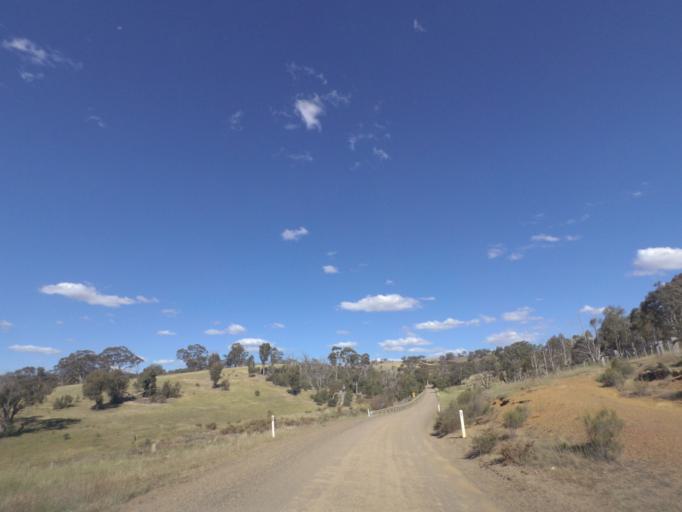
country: AU
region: Victoria
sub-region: Hume
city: Craigieburn
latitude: -37.4130
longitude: 144.9151
